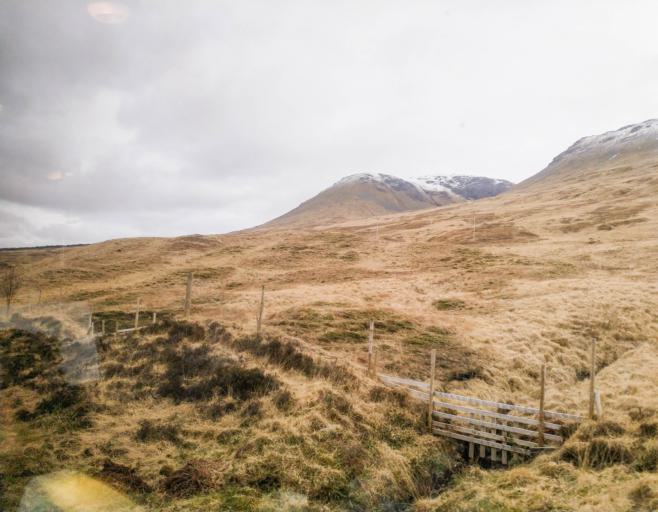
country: GB
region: Scotland
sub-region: Highland
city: Spean Bridge
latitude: 56.5087
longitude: -4.7597
